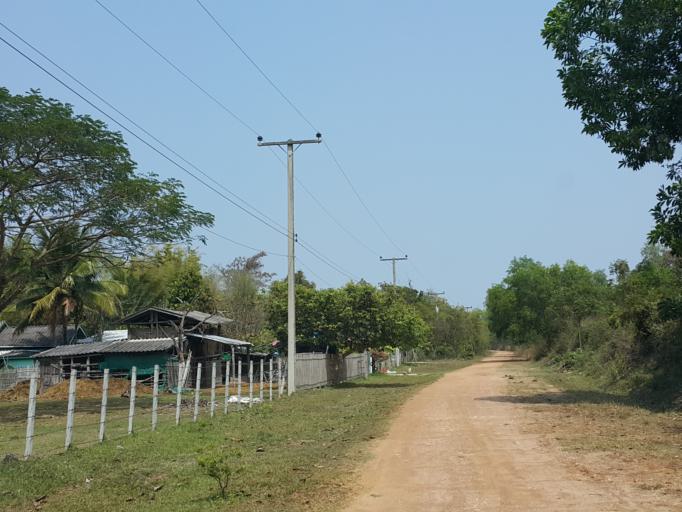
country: TH
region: Lampang
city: Hang Chat
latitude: 18.3056
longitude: 99.4165
